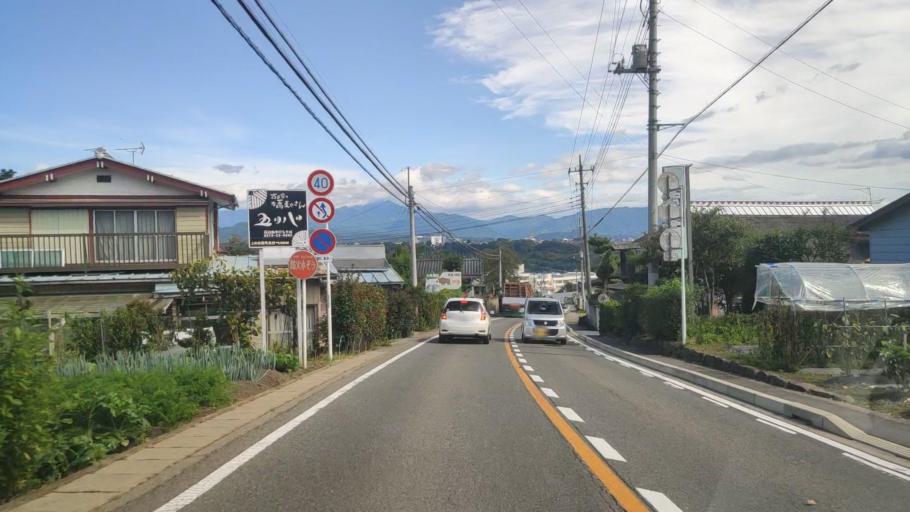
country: JP
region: Gunma
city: Numata
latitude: 36.6272
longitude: 139.0291
